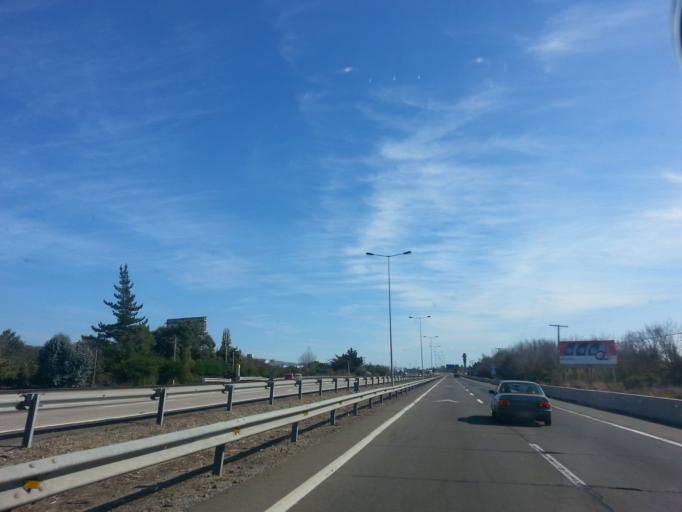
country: CL
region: Valparaiso
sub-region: Provincia de Marga Marga
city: Villa Alemana
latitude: -33.3338
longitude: -71.3813
